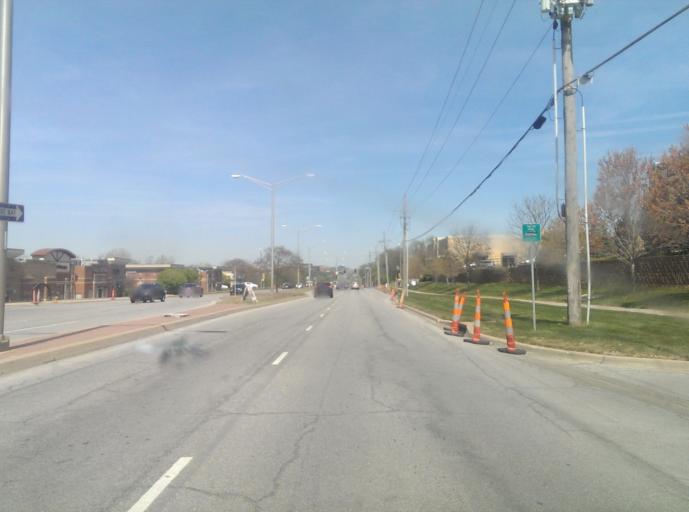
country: US
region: Kansas
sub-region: Johnson County
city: Lenexa
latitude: 38.8846
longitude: -94.6679
